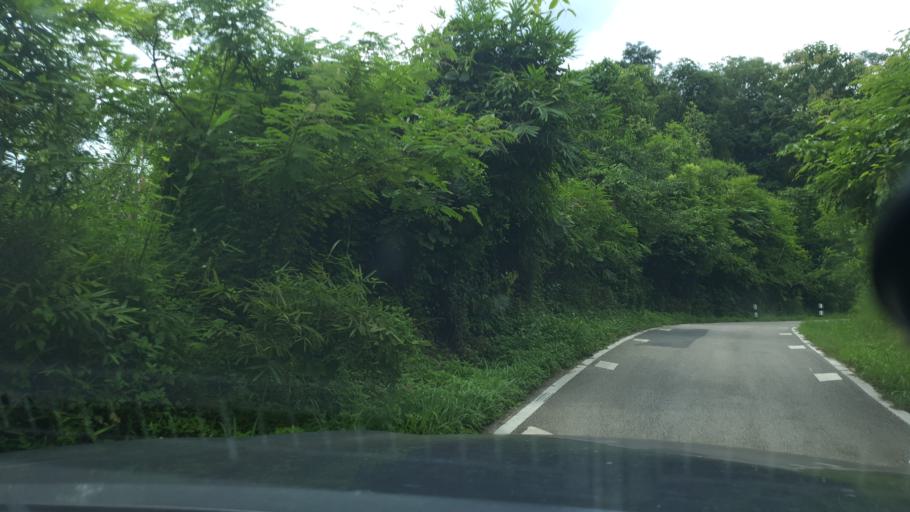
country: TH
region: Lampang
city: Hang Chat
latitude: 18.4178
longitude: 99.2638
